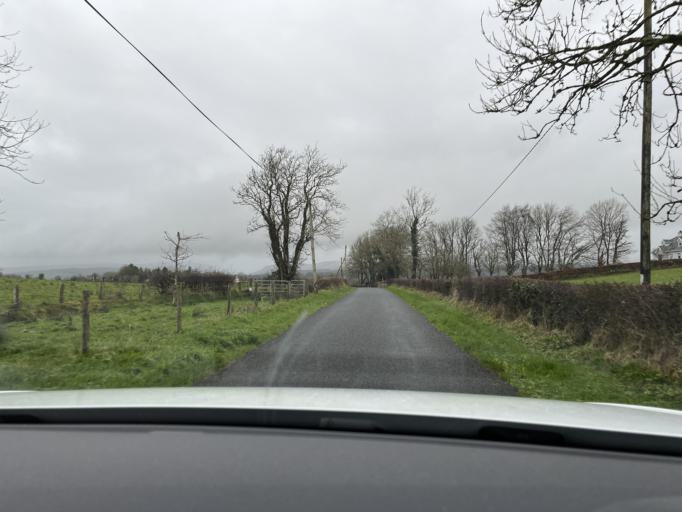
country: IE
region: Connaught
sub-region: County Leitrim
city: Manorhamilton
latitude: 54.2965
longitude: -8.1404
